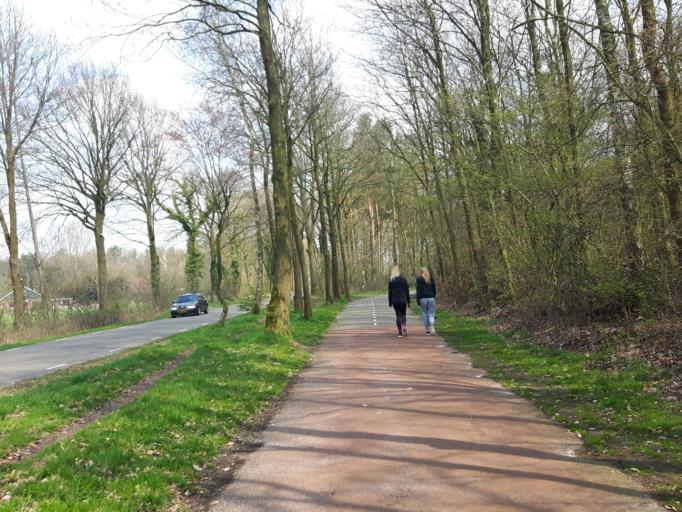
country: NL
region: Overijssel
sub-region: Gemeente Enschede
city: Enschede
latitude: 52.1846
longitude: 6.8423
